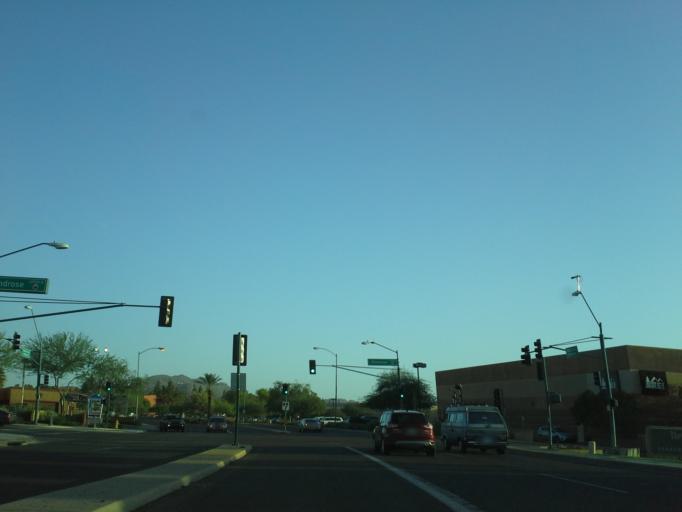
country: US
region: Arizona
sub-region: Maricopa County
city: Paradise Valley
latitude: 33.6028
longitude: -111.9884
